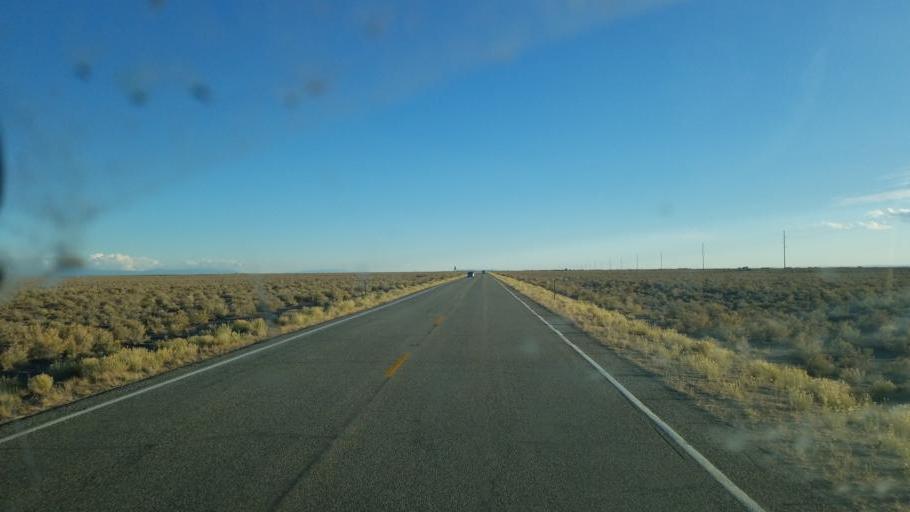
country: US
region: Colorado
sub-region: Saguache County
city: Center
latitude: 37.8366
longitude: -105.8905
